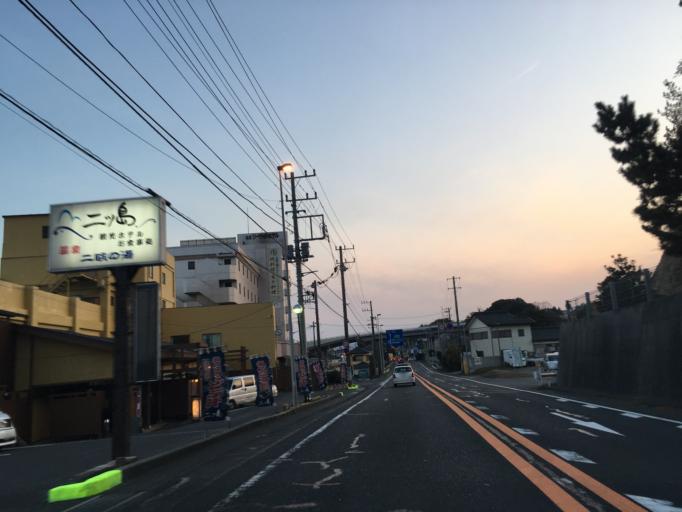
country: JP
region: Ibaraki
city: Kitaibaraki
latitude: 36.8071
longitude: 140.7617
